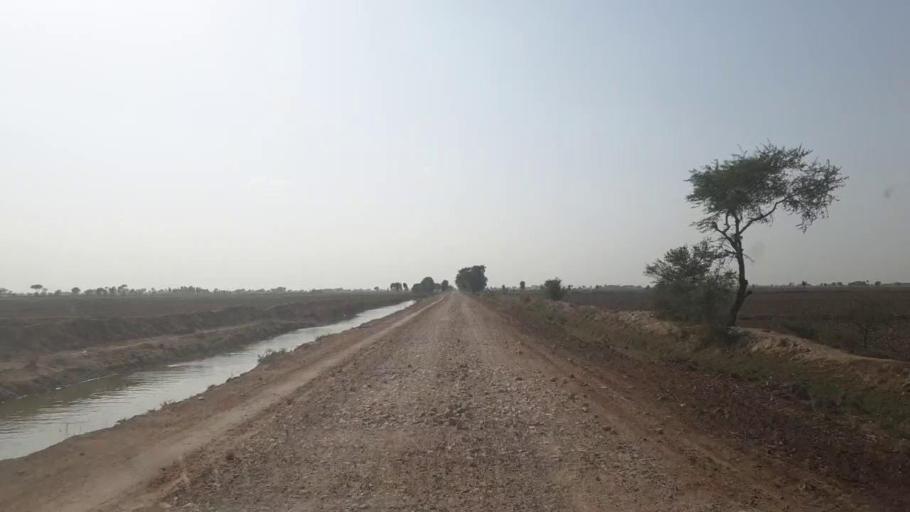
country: PK
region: Sindh
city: Kario
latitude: 24.5589
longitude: 68.5210
